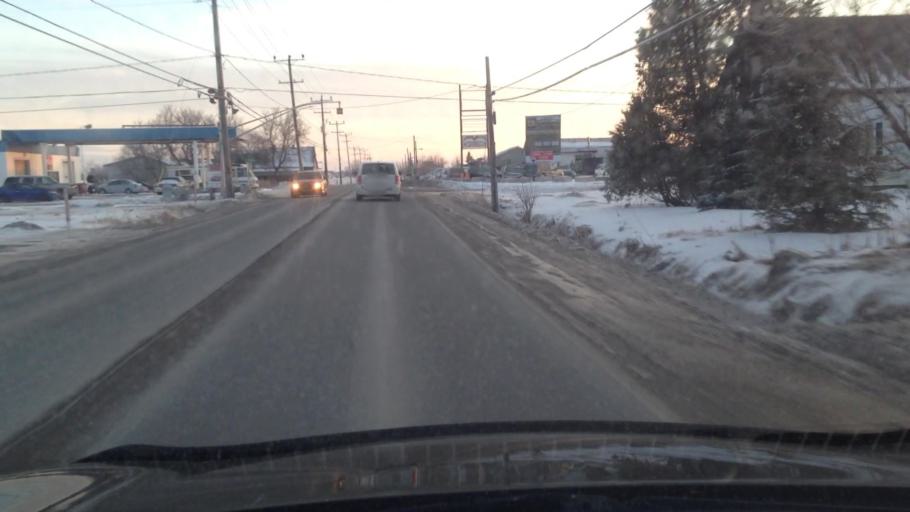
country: CA
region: Quebec
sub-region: Lanaudiere
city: Saint-Lin-Laurentides
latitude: 45.8786
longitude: -73.7576
